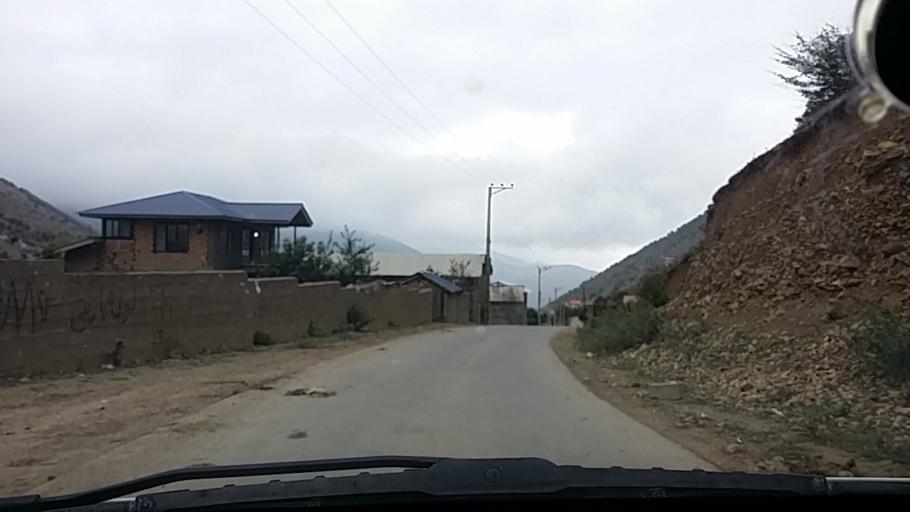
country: IR
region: Mazandaran
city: `Abbasabad
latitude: 36.4682
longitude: 51.1396
